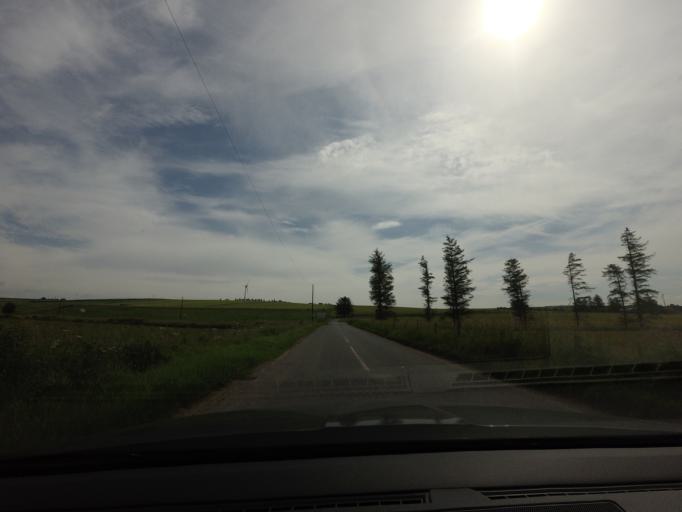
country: GB
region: Scotland
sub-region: Aberdeenshire
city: Turriff
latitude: 57.5589
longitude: -2.3102
